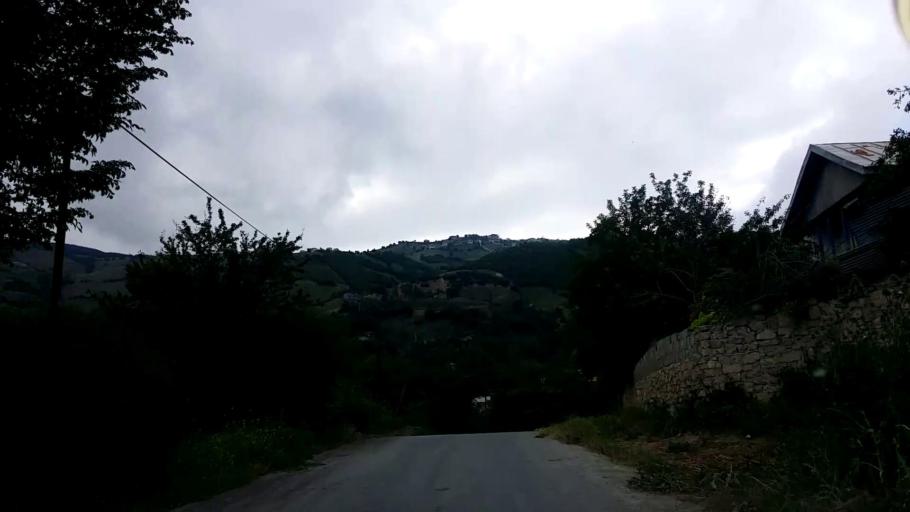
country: IR
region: Mazandaran
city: Chalus
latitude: 36.5539
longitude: 51.2776
